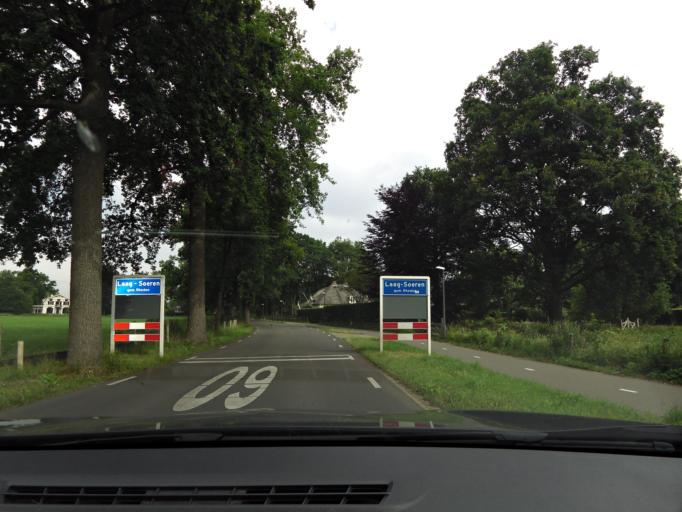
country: NL
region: Gelderland
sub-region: Gemeente Rheden
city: Dieren
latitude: 52.0784
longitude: 6.0820
